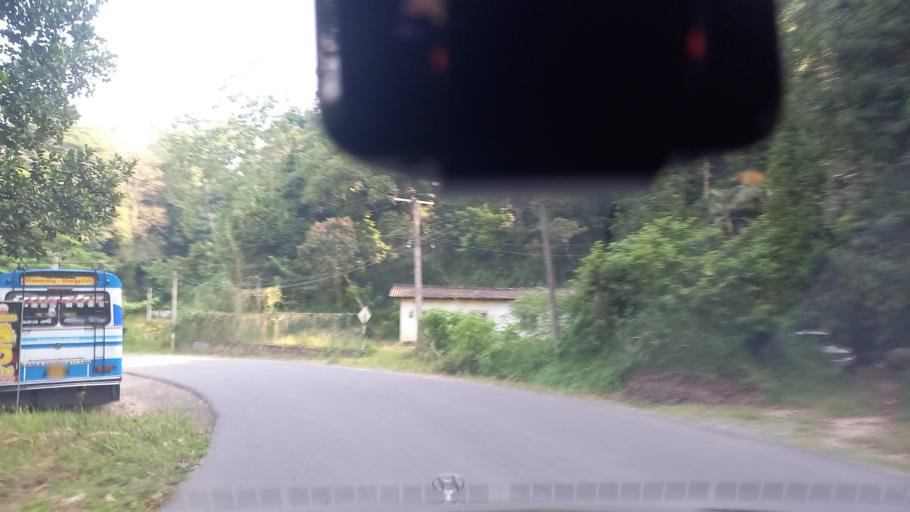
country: LK
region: Central
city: Gampola
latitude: 7.2290
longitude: 80.6038
